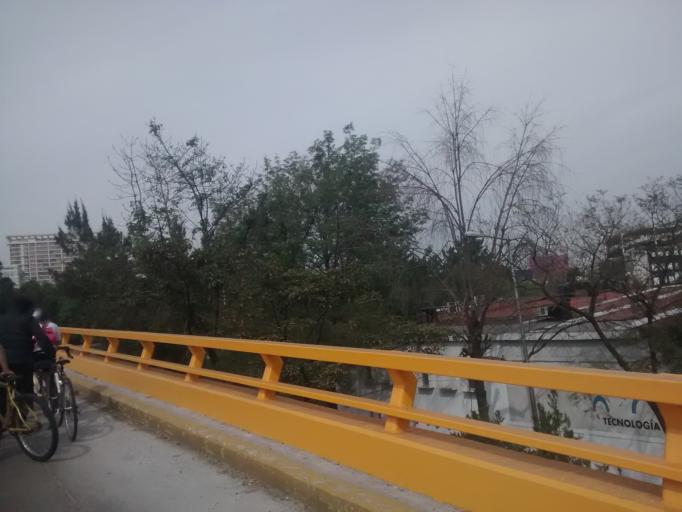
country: MX
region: Mexico City
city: Coyoacan
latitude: 19.3583
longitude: -99.1628
